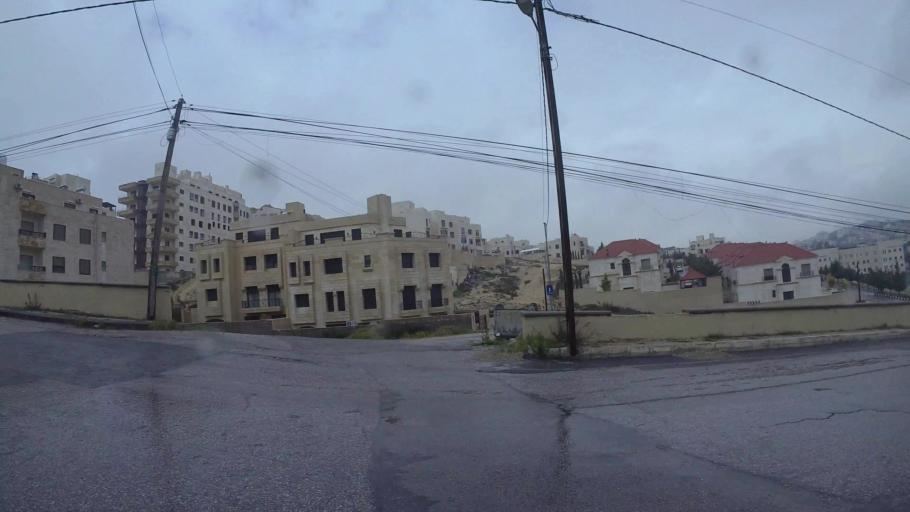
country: JO
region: Amman
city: Al Jubayhah
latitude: 32.0063
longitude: 35.8297
